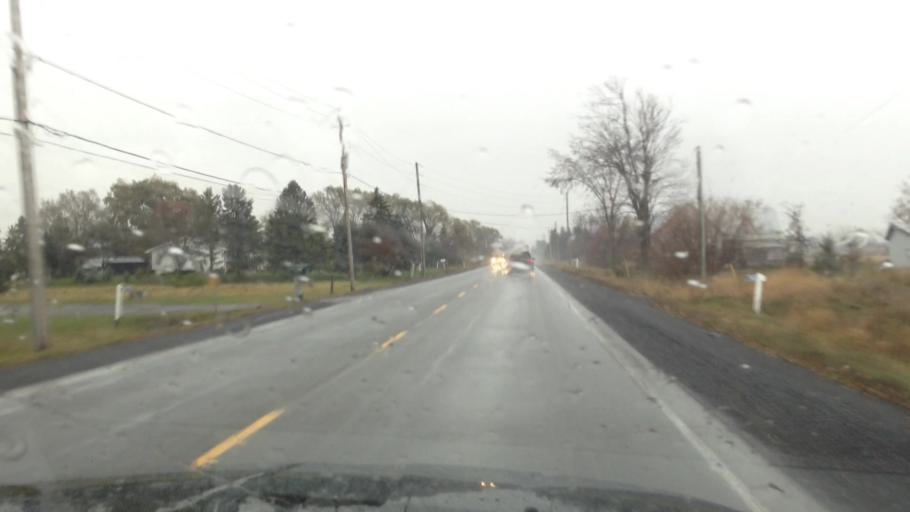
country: CA
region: Ontario
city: Bourget
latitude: 45.3102
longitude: -75.3341
